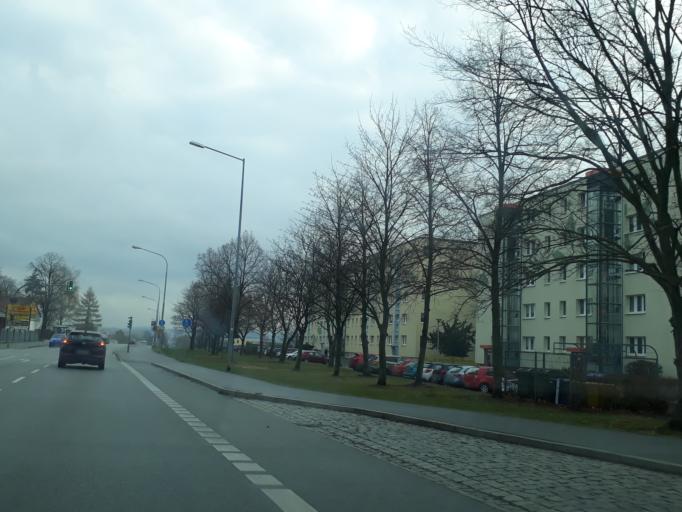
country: DE
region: Saxony
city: Bautzen
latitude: 51.1774
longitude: 14.4566
